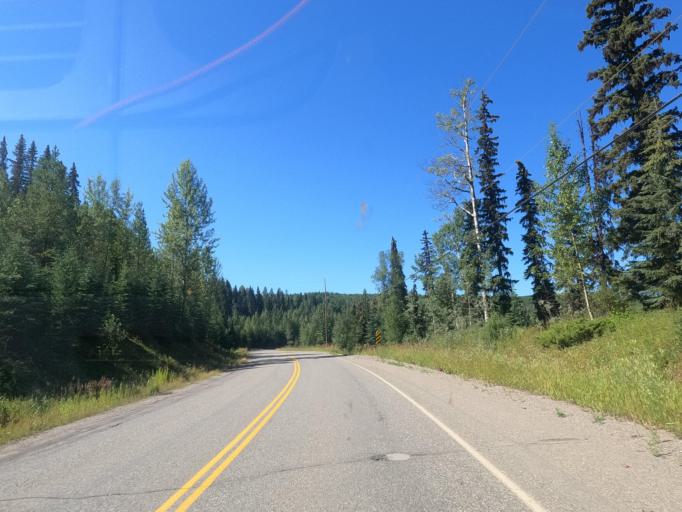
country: CA
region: British Columbia
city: Quesnel
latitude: 53.0530
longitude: -122.1797
